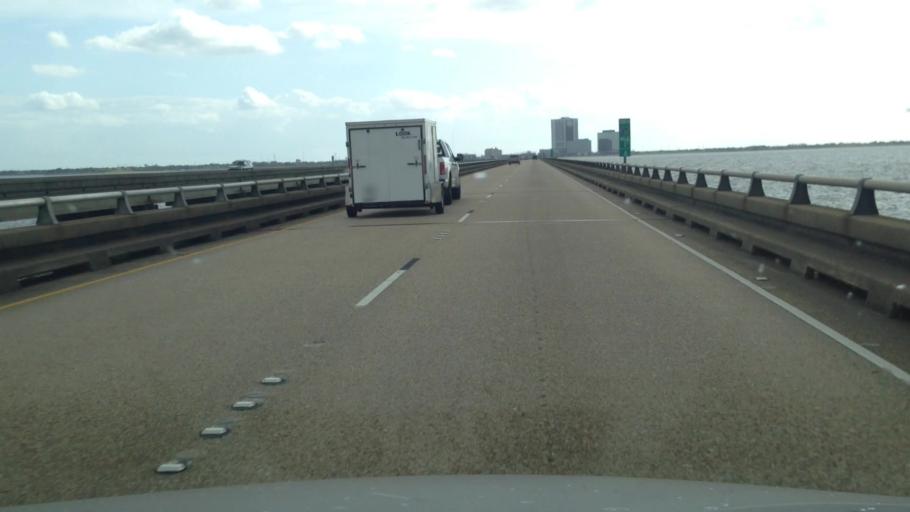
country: US
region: Louisiana
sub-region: Jefferson Parish
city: Metairie
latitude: 30.0450
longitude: -90.1500
